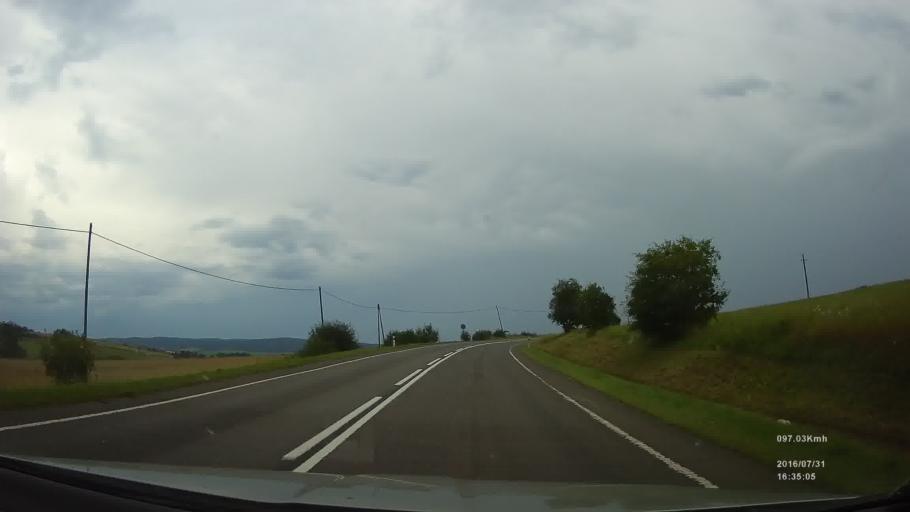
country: SK
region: Presovsky
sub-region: Okres Bardejov
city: Bardejov
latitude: 49.1598
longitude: 21.3143
